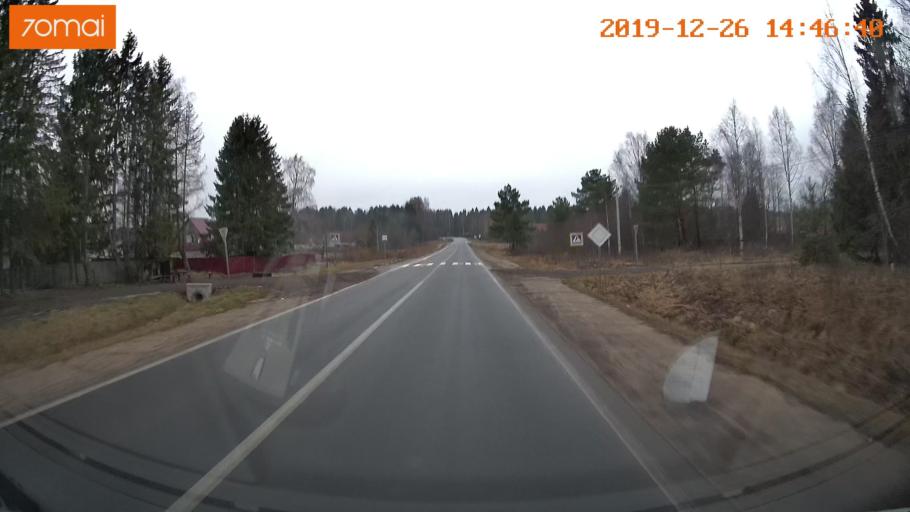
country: RU
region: Jaroslavl
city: Poshekhon'ye
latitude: 58.3382
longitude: 39.0137
